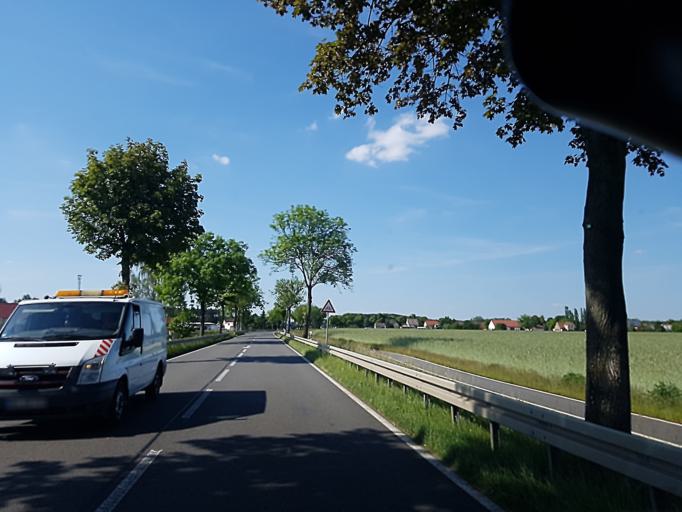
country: DE
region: Brandenburg
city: Schilda
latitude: 51.5726
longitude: 13.3589
